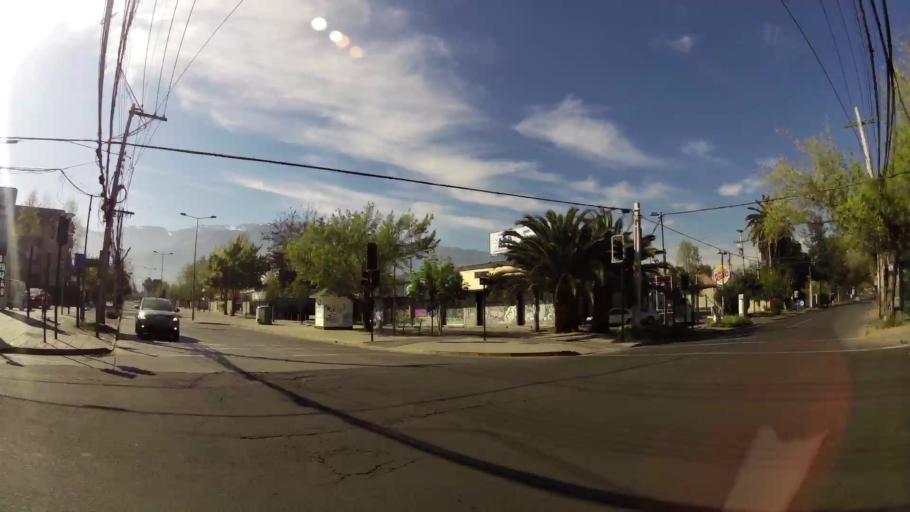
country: CL
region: Santiago Metropolitan
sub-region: Provincia de Santiago
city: Villa Presidente Frei, Nunoa, Santiago, Chile
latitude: -33.4387
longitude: -70.5615
